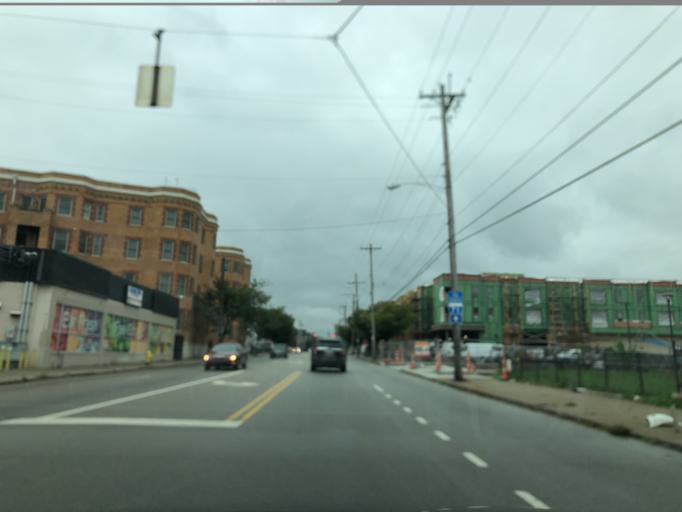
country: US
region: Ohio
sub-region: Hamilton County
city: Saint Bernard
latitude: 39.1463
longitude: -84.4898
